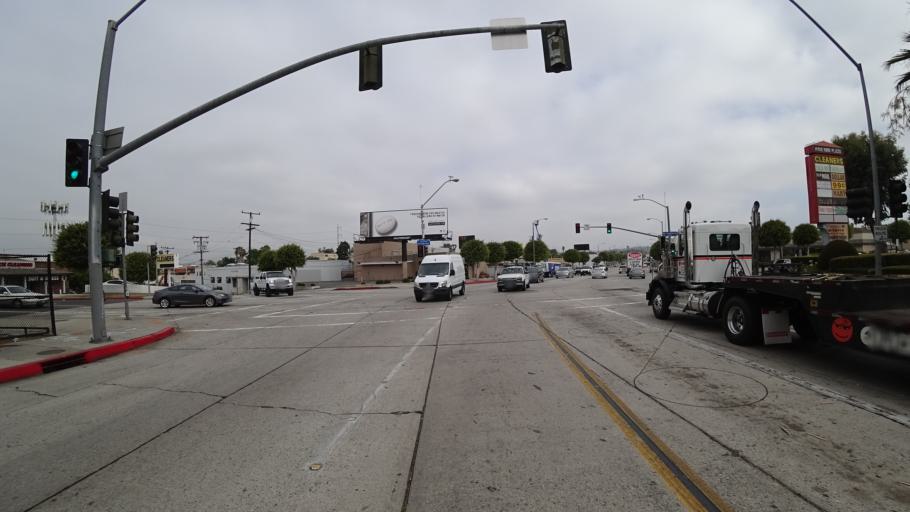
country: US
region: California
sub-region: Los Angeles County
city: Inglewood
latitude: 33.9712
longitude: -118.3574
